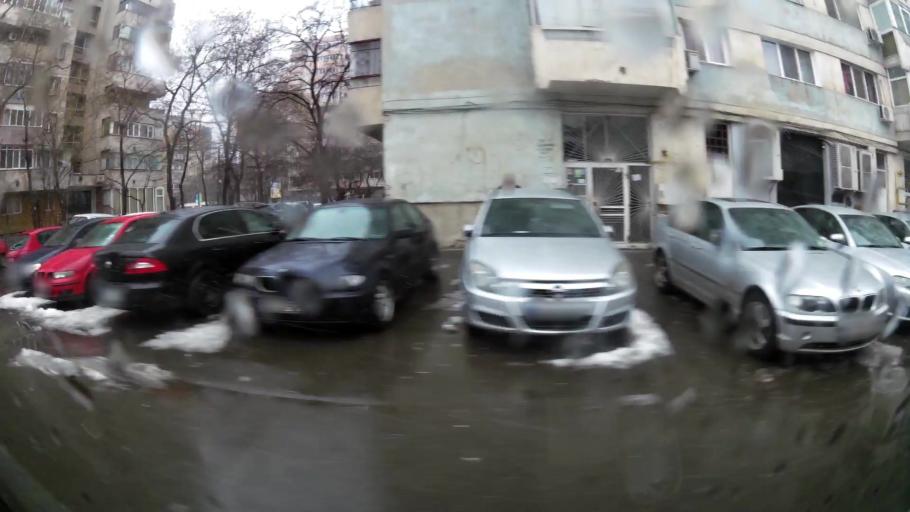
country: RO
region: Ilfov
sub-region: Comuna Chiajna
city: Rosu
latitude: 44.4336
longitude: 26.0185
